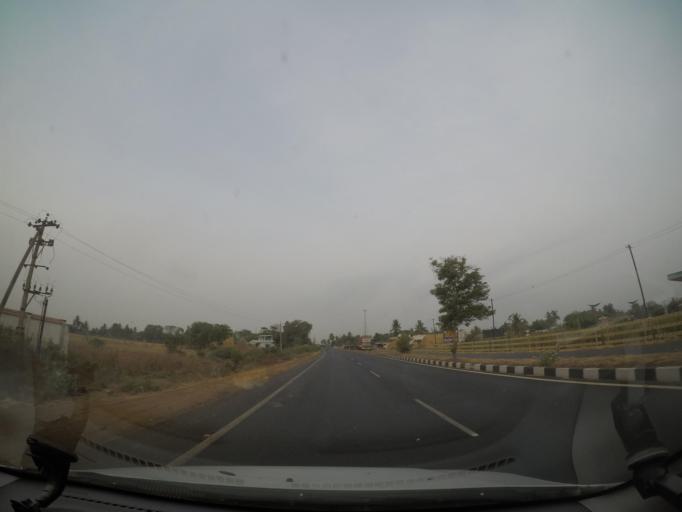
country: IN
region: Andhra Pradesh
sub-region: Krishna
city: Gannavaram
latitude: 16.5995
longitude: 80.8957
